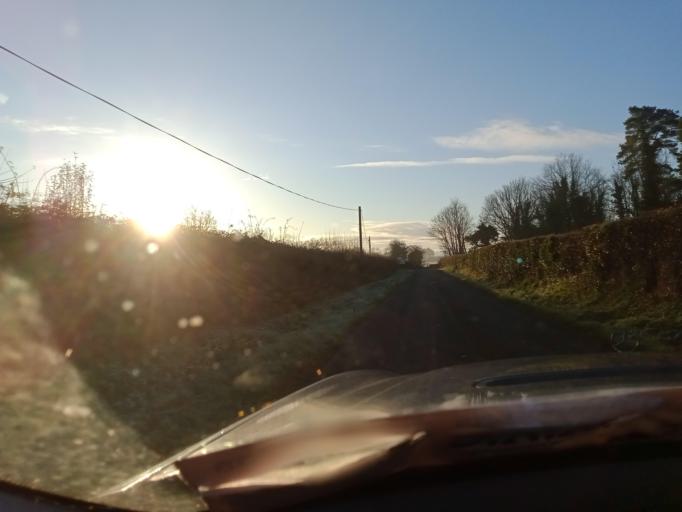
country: IE
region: Leinster
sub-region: Kilkenny
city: Callan
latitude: 52.5309
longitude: -7.4287
